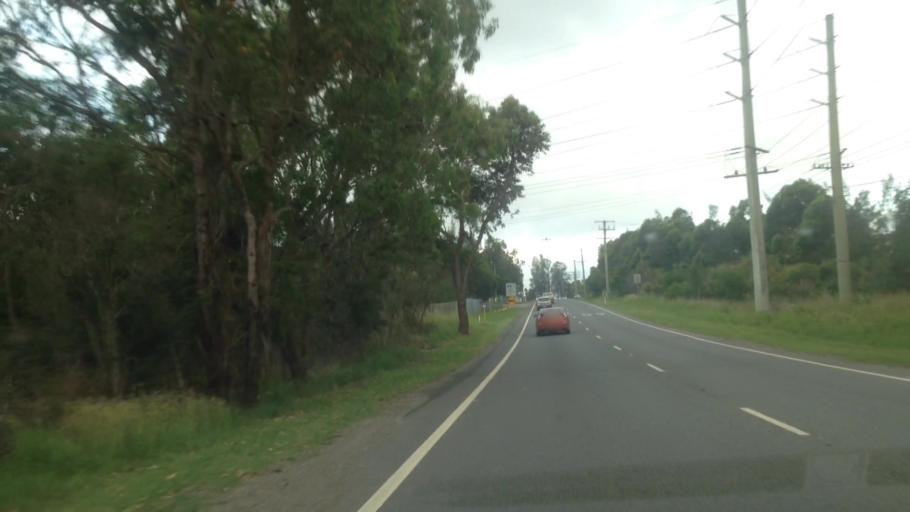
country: AU
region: New South Wales
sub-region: Lake Macquarie Shire
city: Dora Creek
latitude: -33.1140
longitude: 151.4745
